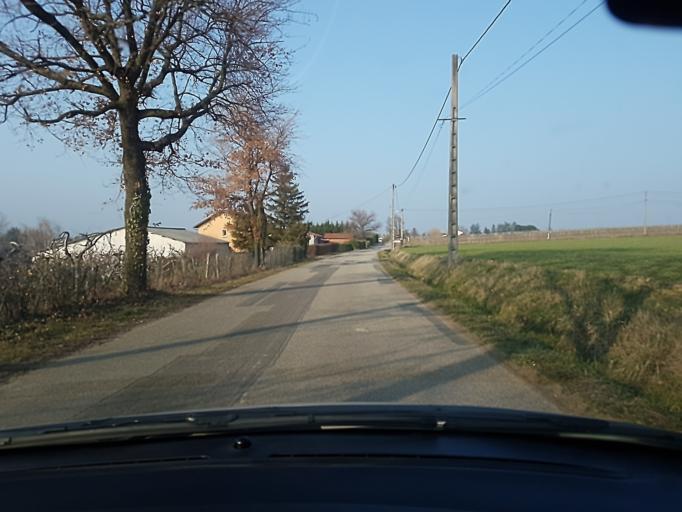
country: FR
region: Rhone-Alpes
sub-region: Departement du Rhone
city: Taluyers
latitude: 45.6321
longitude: 4.7181
